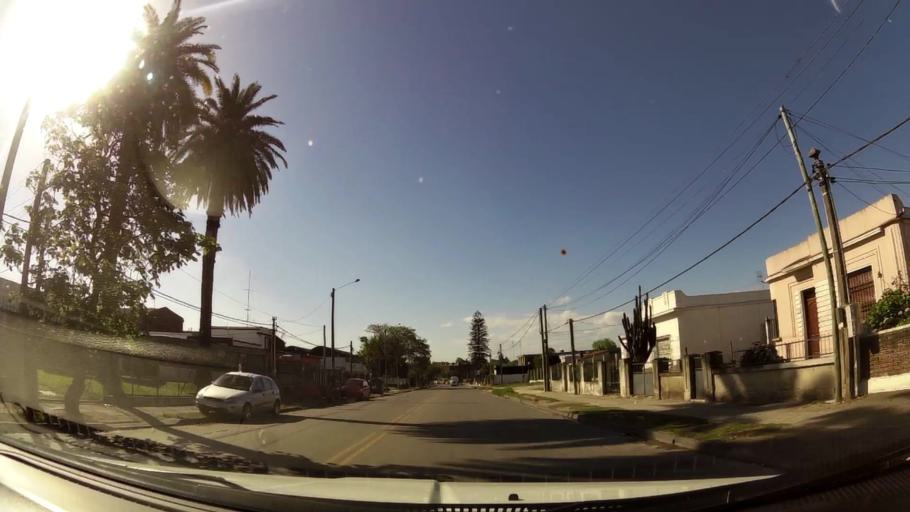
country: UY
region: Montevideo
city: Montevideo
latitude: -34.8353
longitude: -56.1506
